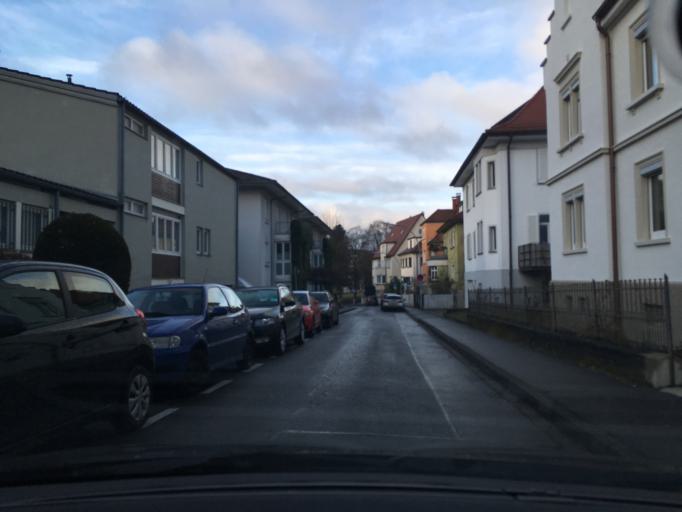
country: DE
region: Baden-Wuerttemberg
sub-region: Tuebingen Region
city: Ravensburg
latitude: 47.7803
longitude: 9.6192
